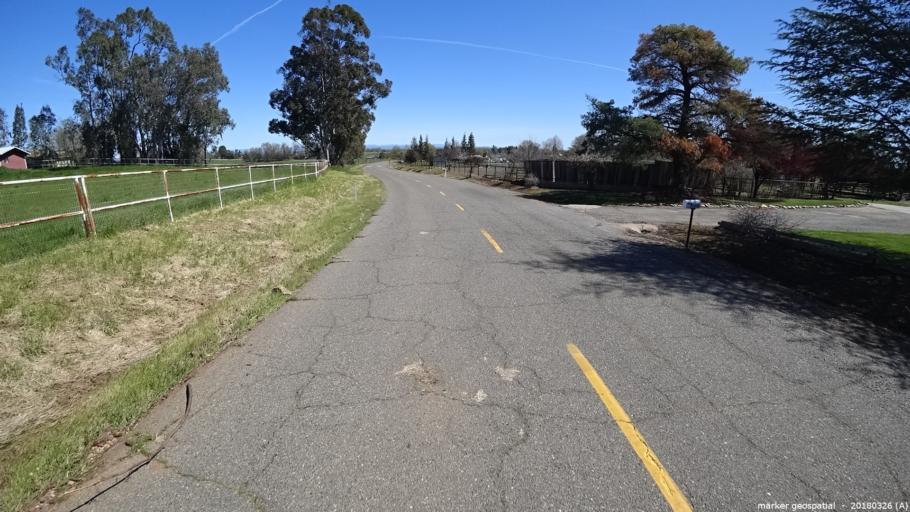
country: US
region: California
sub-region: Sacramento County
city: Wilton
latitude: 38.4770
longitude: -121.2299
